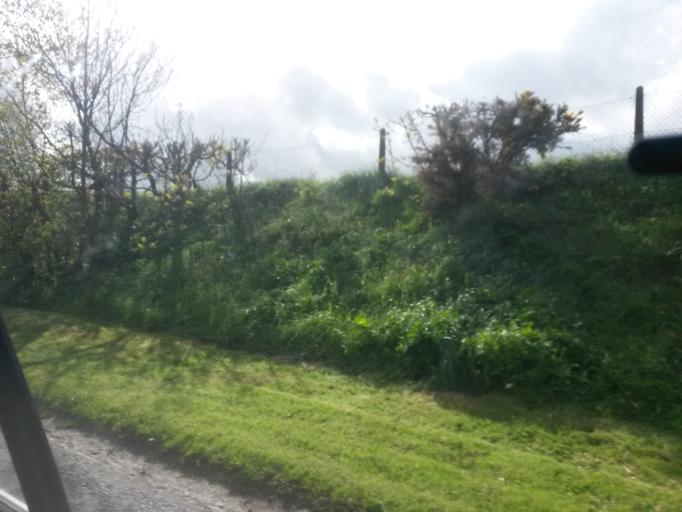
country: IE
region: Leinster
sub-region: Loch Garman
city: Ferns
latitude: 52.6113
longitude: -6.4366
